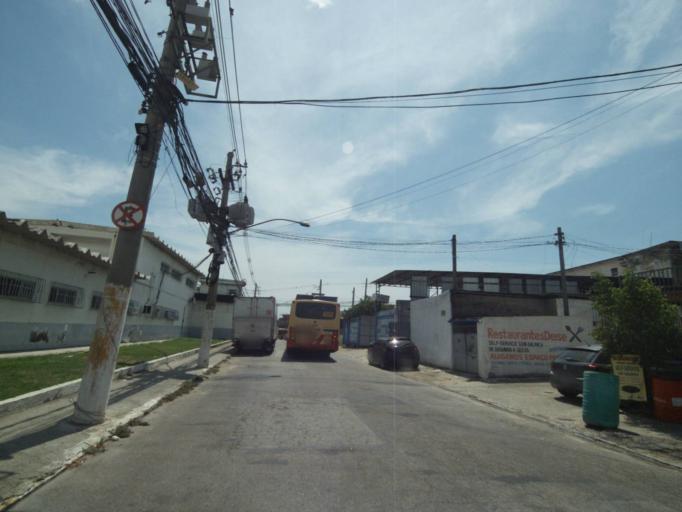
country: BR
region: Rio de Janeiro
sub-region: Duque De Caxias
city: Duque de Caxias
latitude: -22.7973
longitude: -43.2920
